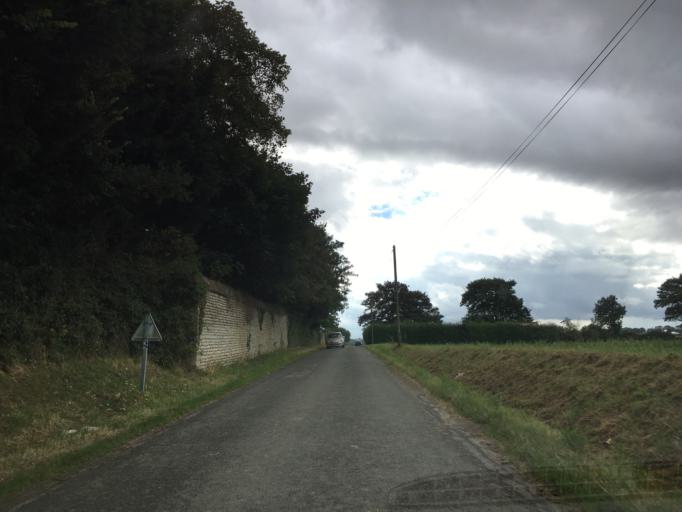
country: FR
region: Lower Normandy
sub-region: Departement du Calvados
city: Lion-sur-Mer
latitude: 49.3040
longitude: -0.3353
